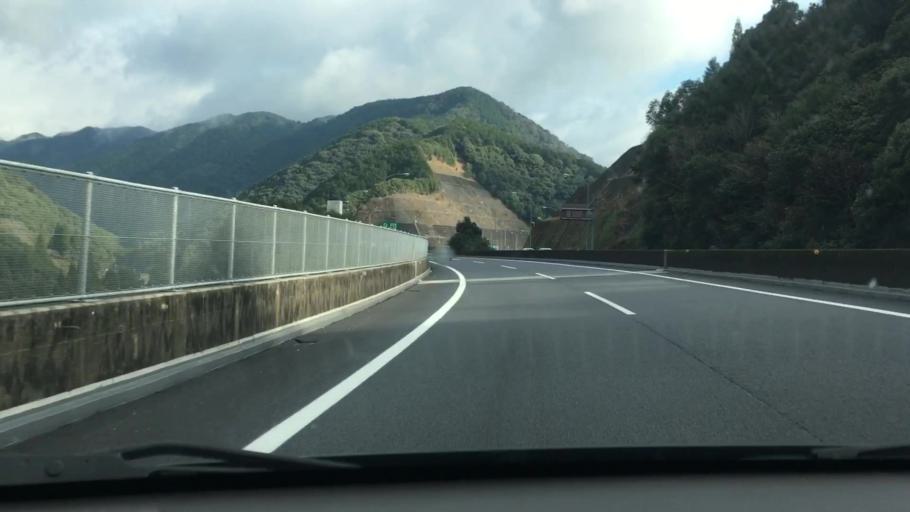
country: JP
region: Kumamoto
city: Yatsushiro
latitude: 32.4436
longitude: 130.6654
